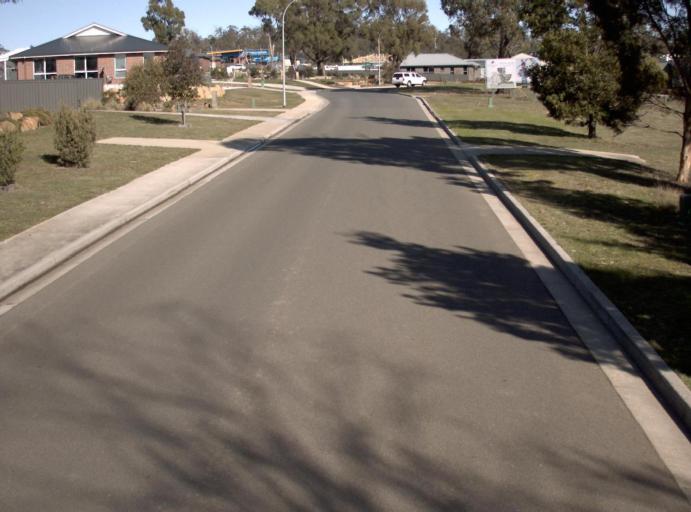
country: AU
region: Tasmania
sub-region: Launceston
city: Summerhill
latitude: -41.4750
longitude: 147.1528
